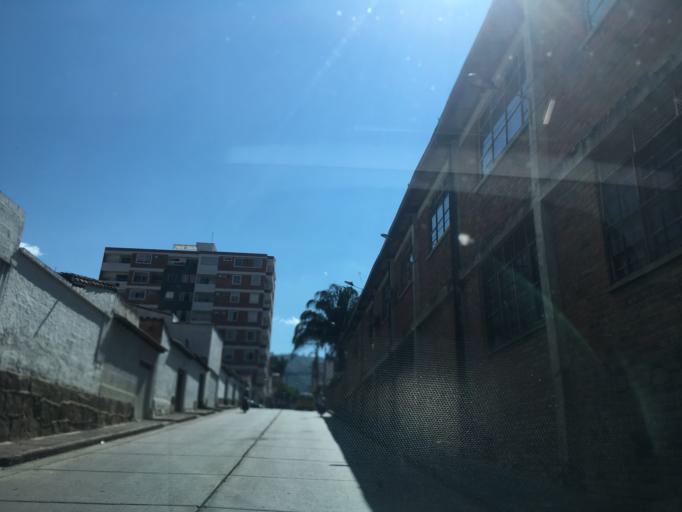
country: CO
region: Santander
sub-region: San Gil
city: San Gil
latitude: 6.5584
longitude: -73.1338
